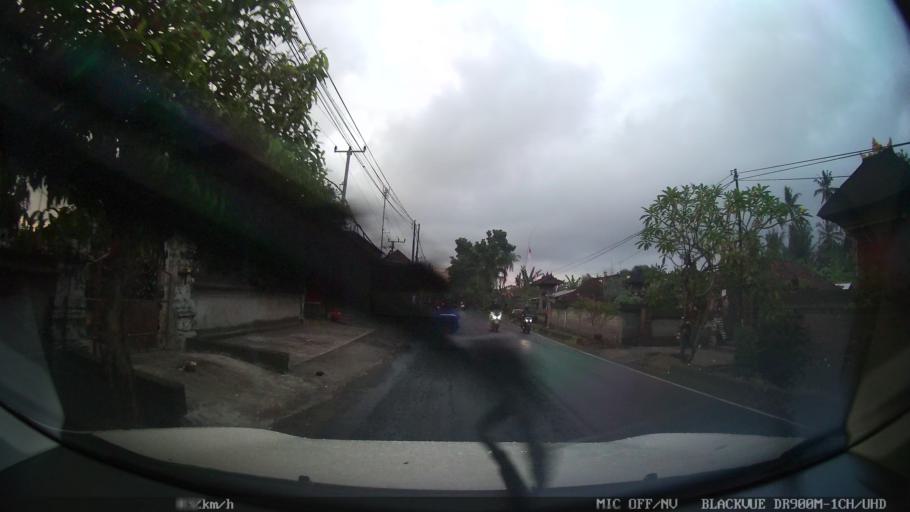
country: ID
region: Bali
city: Banjar Batur
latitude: -8.5980
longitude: 115.2147
